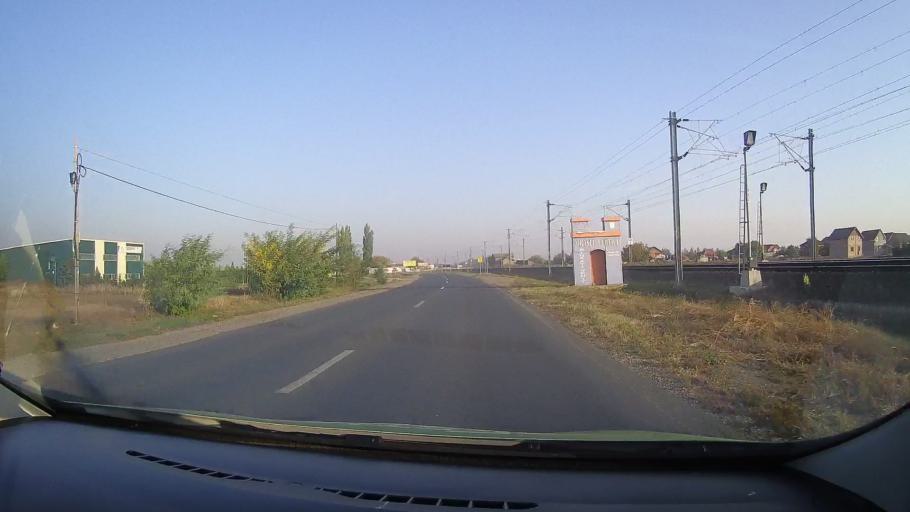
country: RO
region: Arad
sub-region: Comuna Curtici
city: Curtici
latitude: 46.3282
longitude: 21.3053
